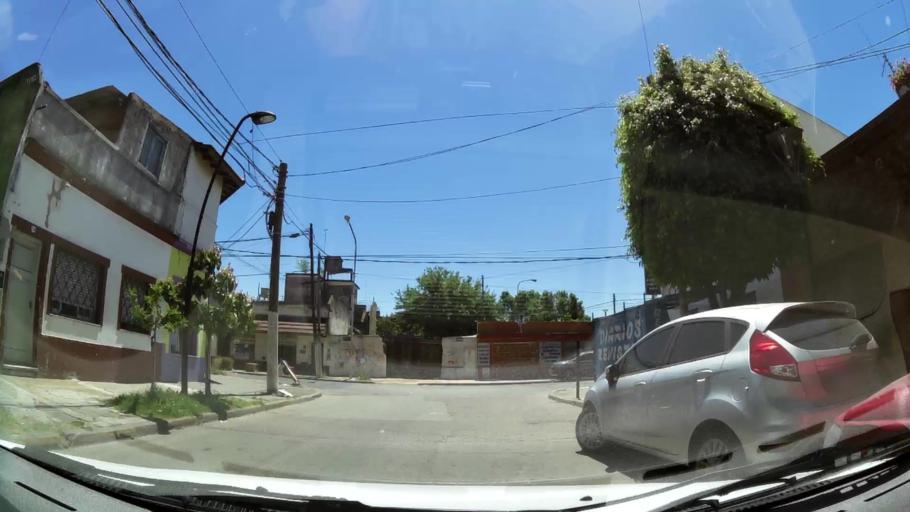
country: AR
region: Buenos Aires
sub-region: Partido de General San Martin
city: General San Martin
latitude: -34.5960
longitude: -58.5347
